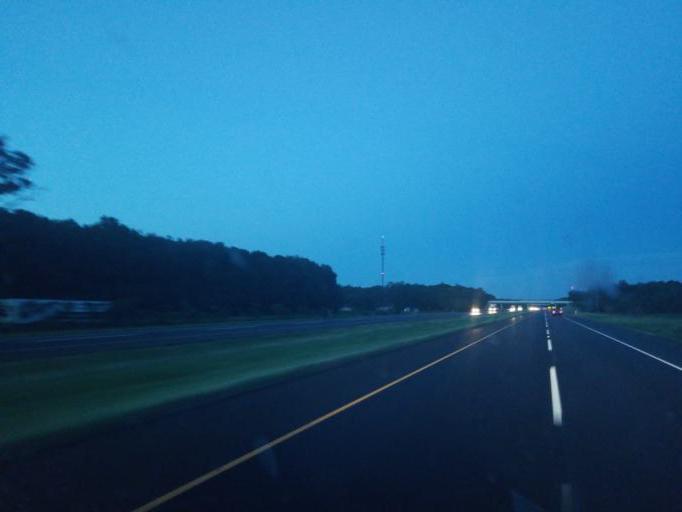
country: US
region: Indiana
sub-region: Saint Joseph County
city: Granger
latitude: 41.7312
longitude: -86.0866
